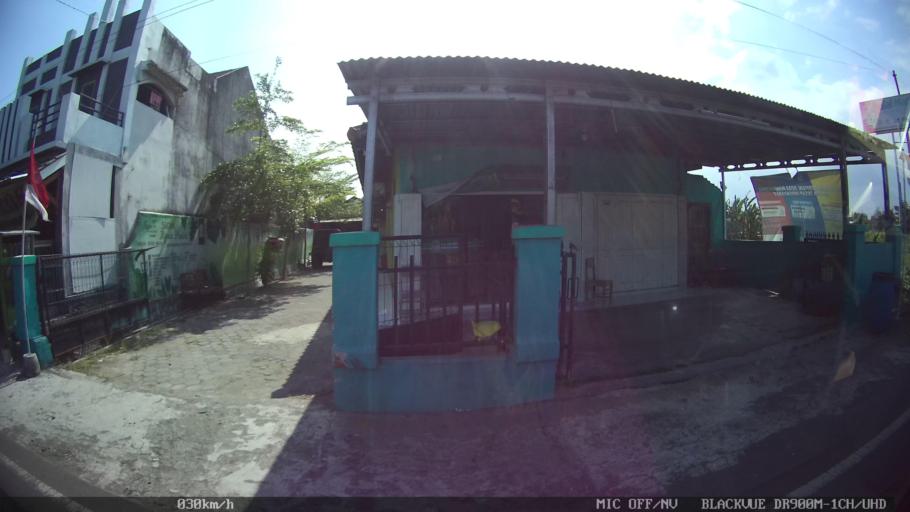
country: ID
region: Daerah Istimewa Yogyakarta
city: Sewon
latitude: -7.8766
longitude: 110.3912
